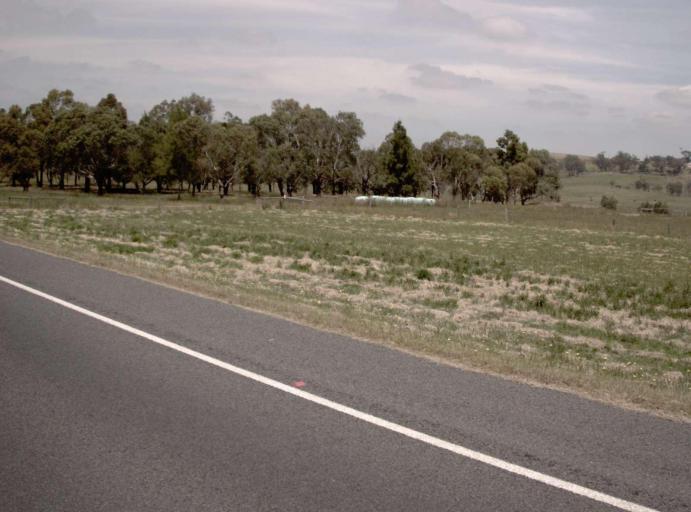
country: AU
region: Victoria
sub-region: Latrobe
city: Traralgon
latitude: -38.2319
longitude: 146.5405
